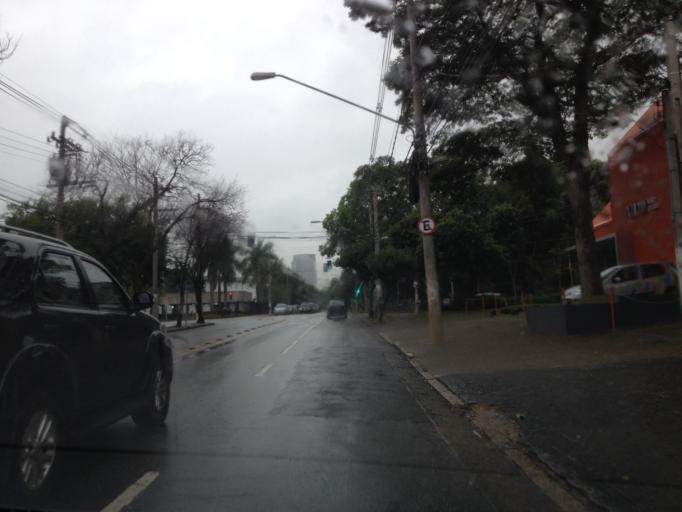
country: BR
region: Sao Paulo
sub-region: Sao Paulo
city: Sao Paulo
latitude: -23.5746
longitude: -46.6774
